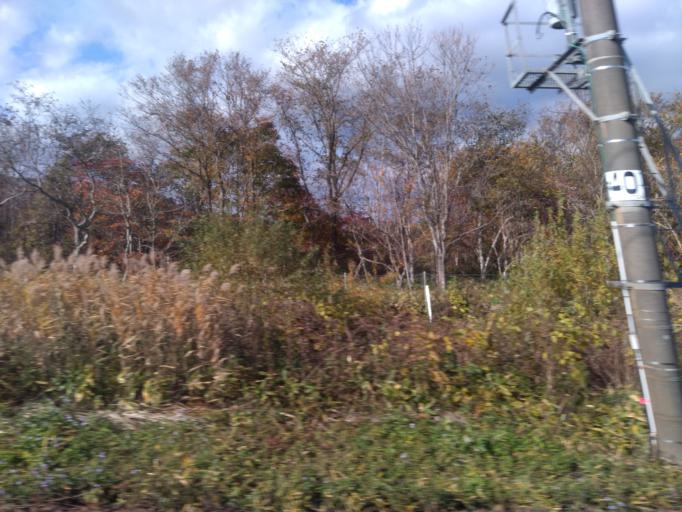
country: JP
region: Hokkaido
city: Shiraoi
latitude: 42.5677
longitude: 141.3844
